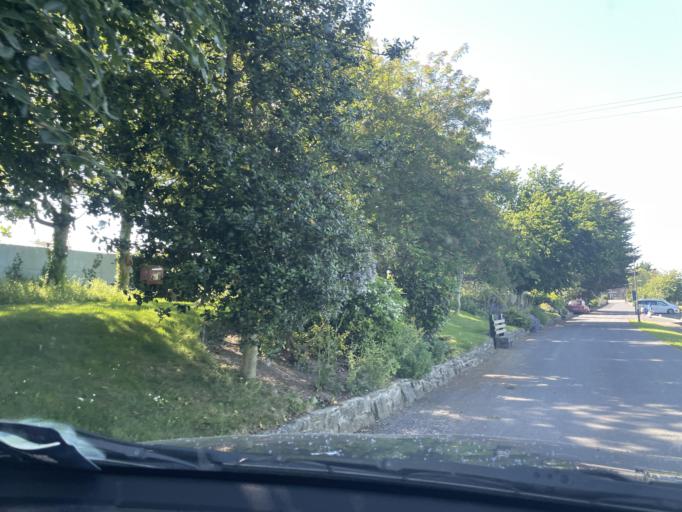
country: IE
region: Leinster
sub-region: County Carlow
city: Bagenalstown
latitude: 52.6292
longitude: -6.9892
